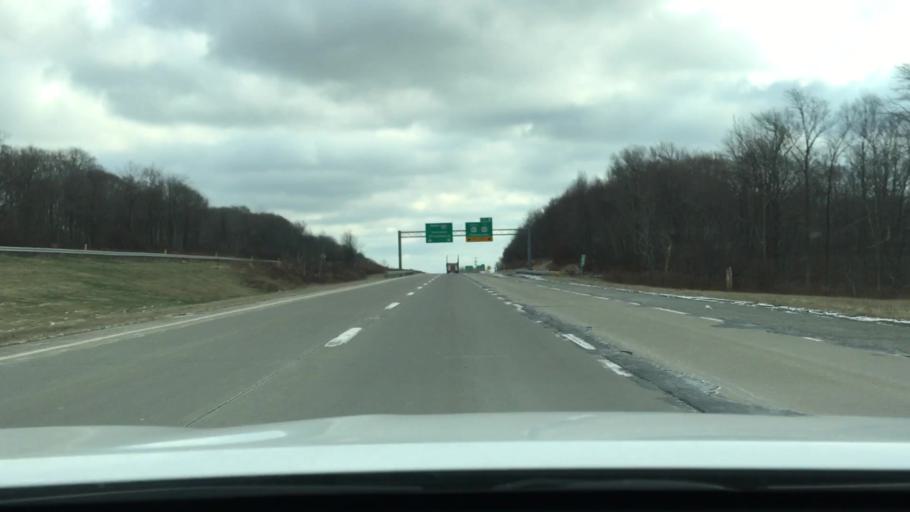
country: US
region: Pennsylvania
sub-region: Monroe County
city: Pocono Pines
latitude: 41.1895
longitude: -75.4418
